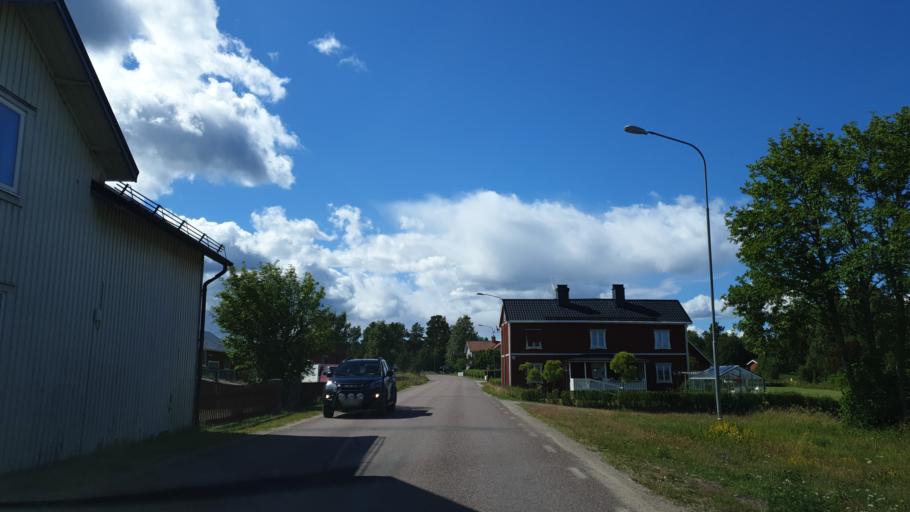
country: SE
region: Gaevleborg
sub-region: Nordanstigs Kommun
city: Bergsjoe
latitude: 62.0522
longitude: 17.1999
